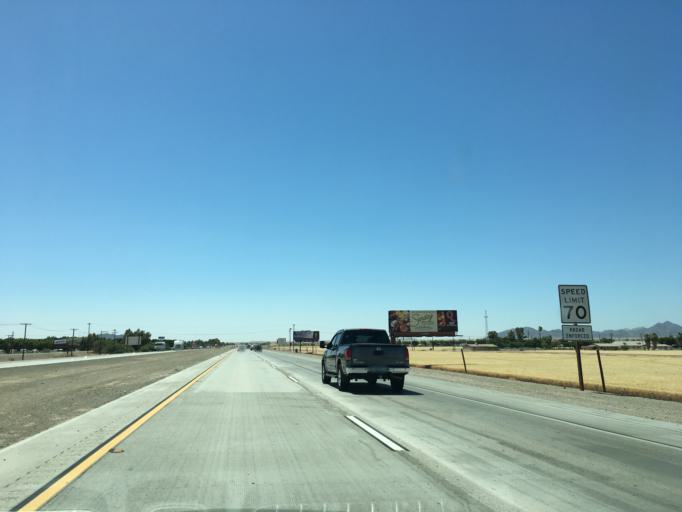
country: US
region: Arizona
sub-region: Yuma County
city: Yuma
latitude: 32.7329
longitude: -114.6293
